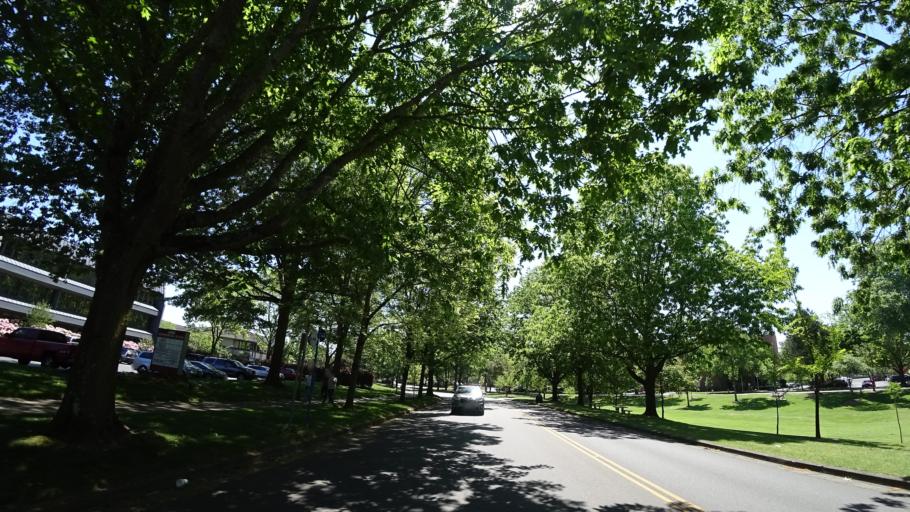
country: US
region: Oregon
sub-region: Washington County
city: Beaverton
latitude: 45.4853
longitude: -122.7953
